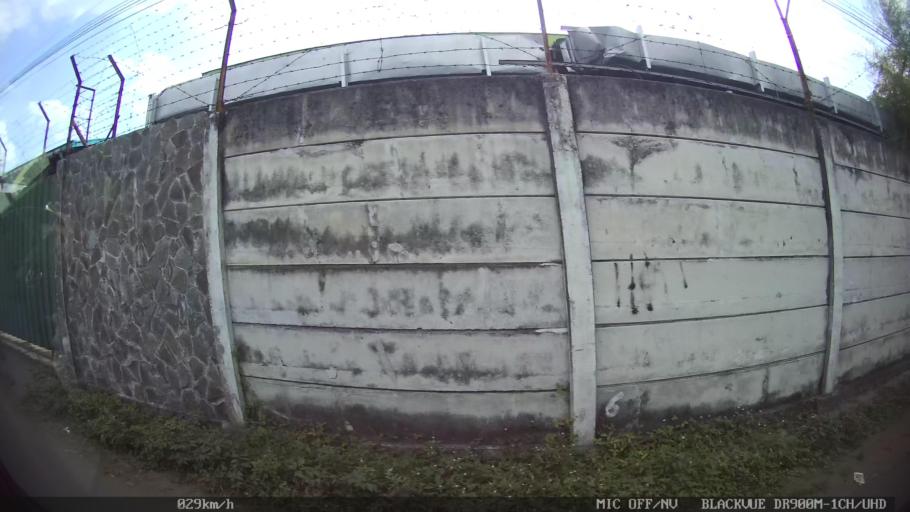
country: ID
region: Daerah Istimewa Yogyakarta
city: Yogyakarta
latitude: -7.7661
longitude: 110.3562
